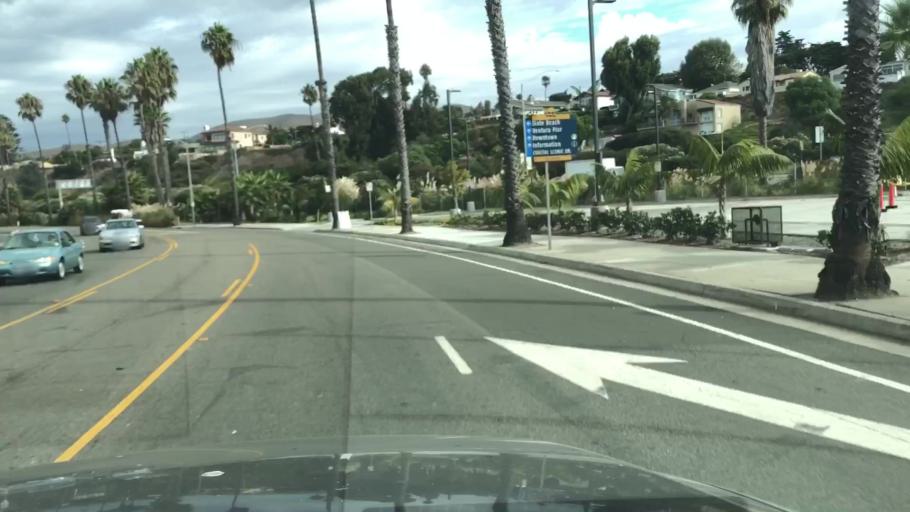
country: US
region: California
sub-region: Ventura County
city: Ventura
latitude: 34.2689
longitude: -119.2732
